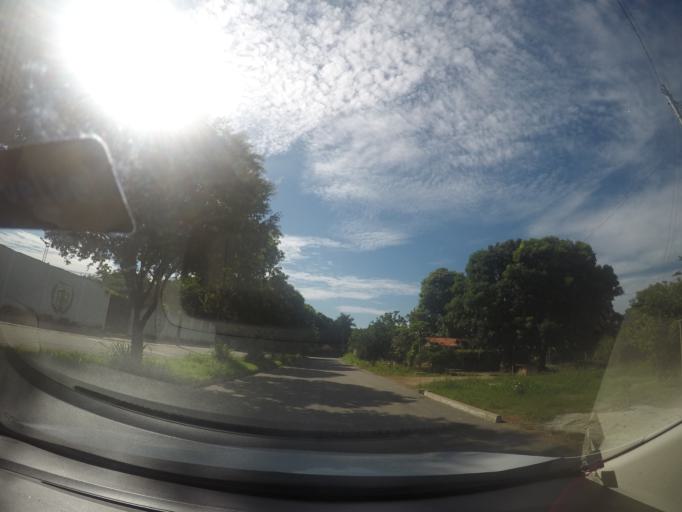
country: BR
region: Goias
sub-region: Goiania
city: Goiania
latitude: -16.6618
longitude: -49.2056
